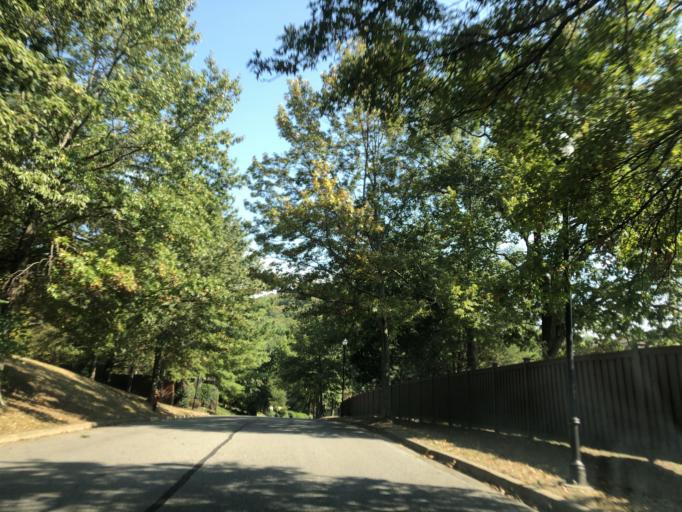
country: US
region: Tennessee
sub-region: Davidson County
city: Oak Hill
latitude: 36.0918
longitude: -86.8137
